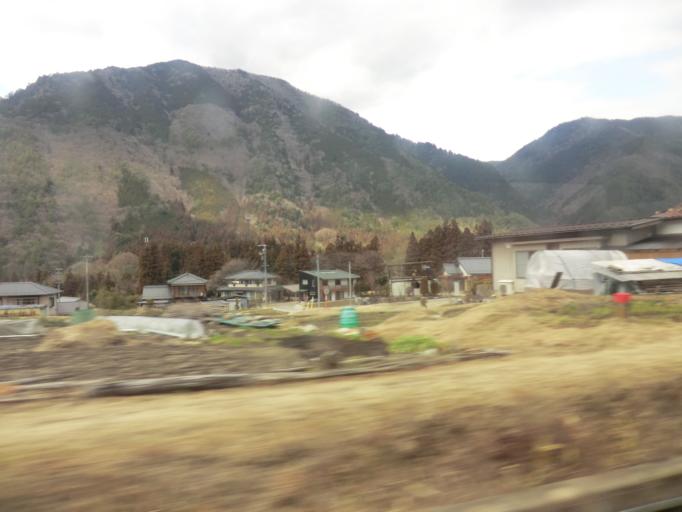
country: JP
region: Gifu
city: Nakatsugawa
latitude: 35.6699
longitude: 137.6315
